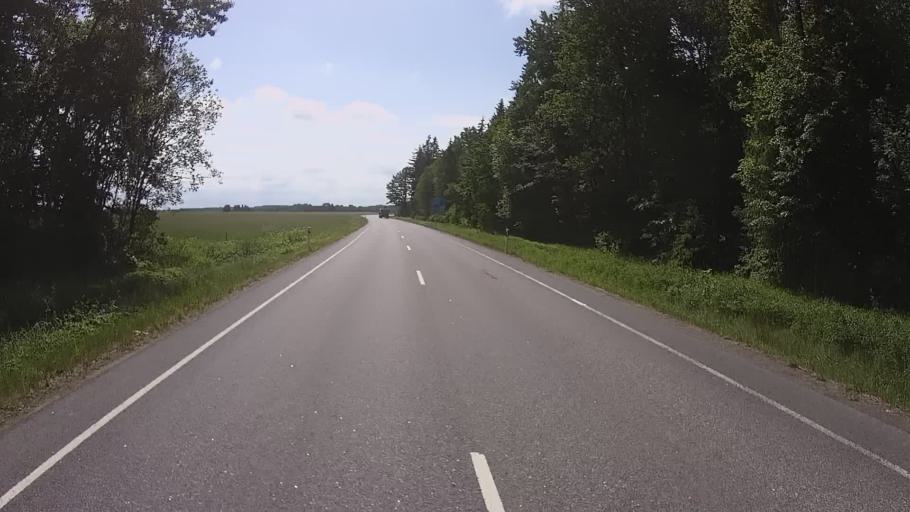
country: EE
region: Tartu
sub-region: Tartu linn
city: Tartu
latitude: 58.3719
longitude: 26.8839
